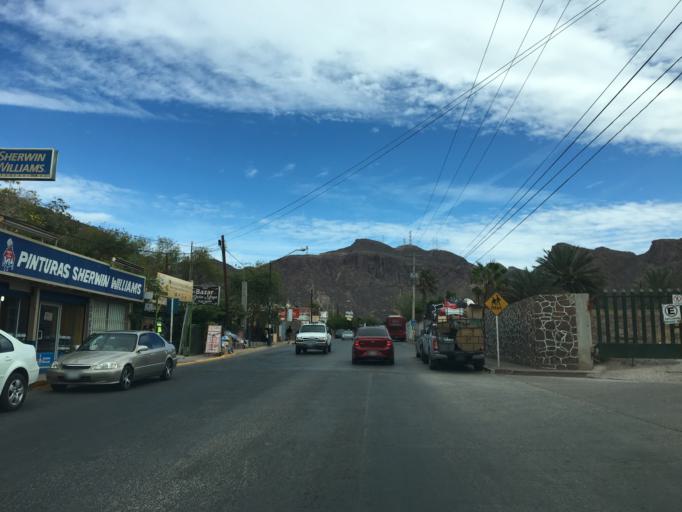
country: MX
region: Sonora
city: Heroica Guaymas
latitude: 27.9183
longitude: -110.9025
